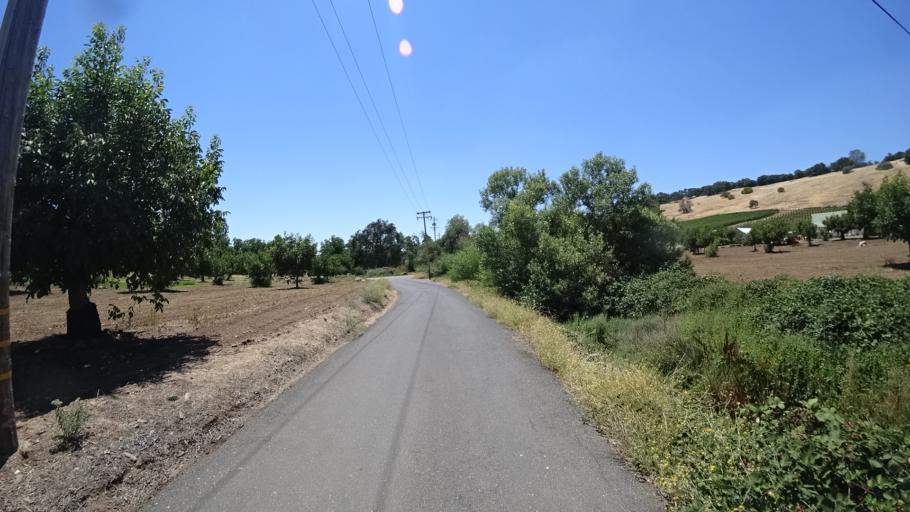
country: US
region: California
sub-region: Calaveras County
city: Murphys
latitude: 38.1042
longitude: -120.4989
